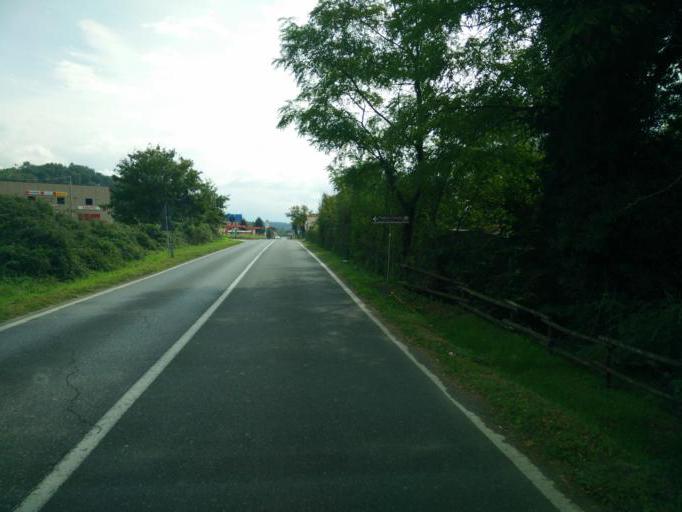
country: IT
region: Tuscany
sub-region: Provincia di Massa-Carrara
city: Pontremoli
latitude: 44.3626
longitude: 9.8969
